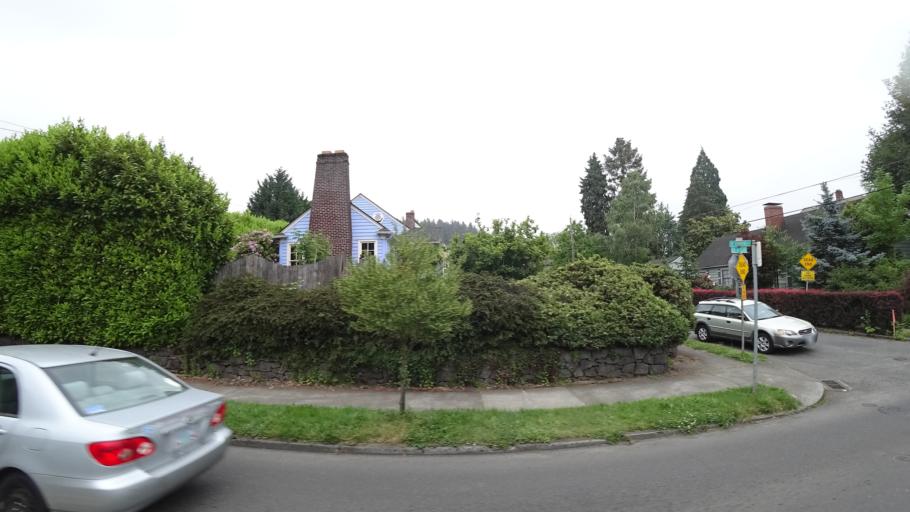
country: US
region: Oregon
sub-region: Multnomah County
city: Lents
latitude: 45.5096
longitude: -122.6018
